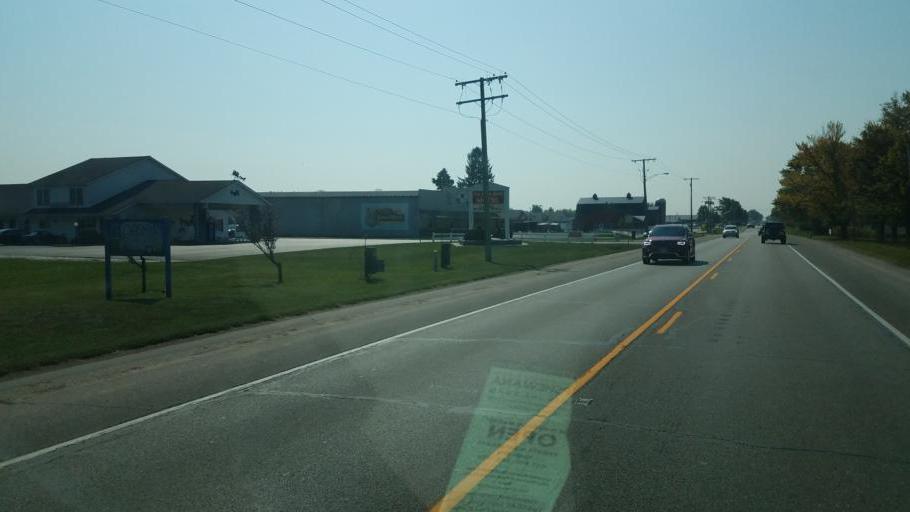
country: US
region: Indiana
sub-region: Elkhart County
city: Middlebury
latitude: 41.6617
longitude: -85.5804
